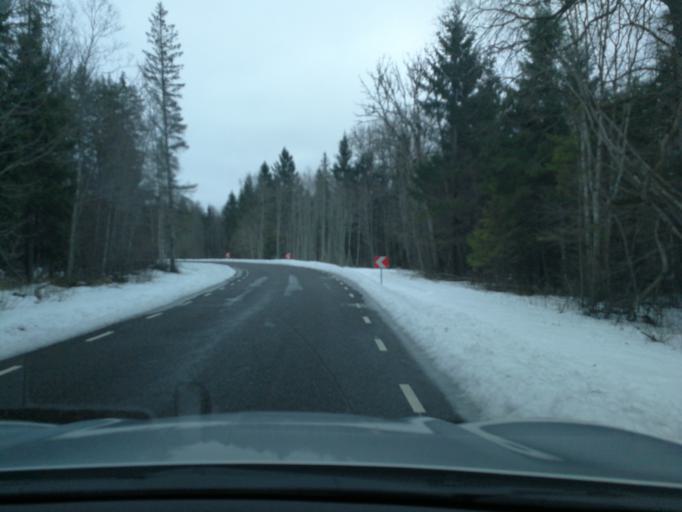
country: EE
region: Harju
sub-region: Rae vald
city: Vaida
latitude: 59.2379
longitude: 24.9210
